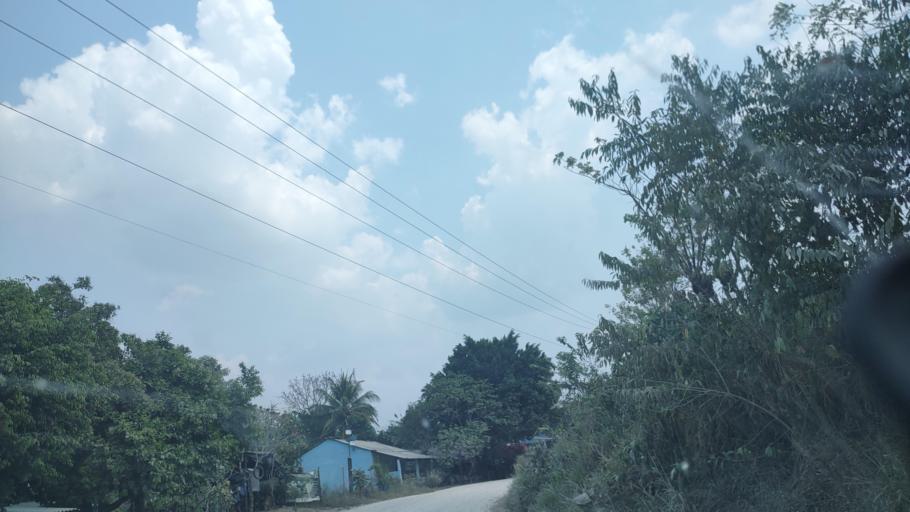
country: MX
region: Tabasco
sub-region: Huimanguillo
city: Francisco Rueda
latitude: 17.6008
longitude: -93.9001
